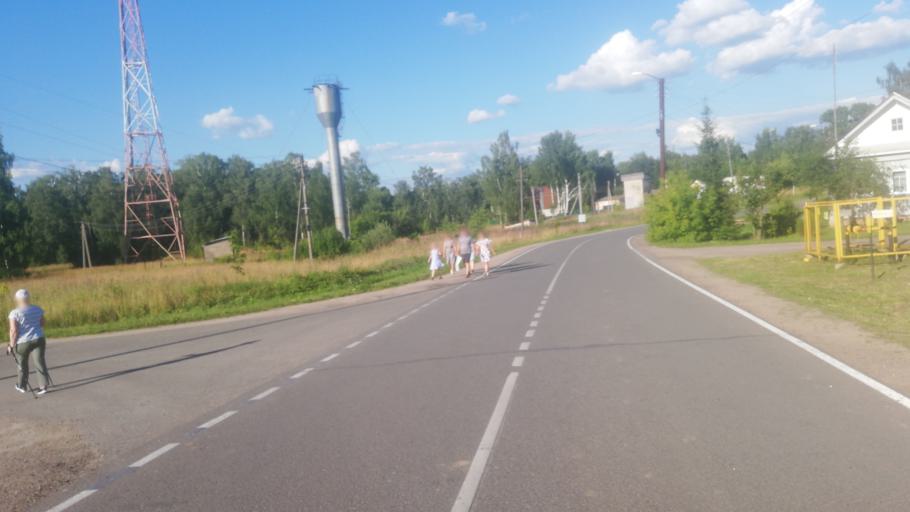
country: RU
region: Ivanovo
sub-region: Privolzhskiy Rayon
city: Ples
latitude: 57.4571
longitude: 41.4952
